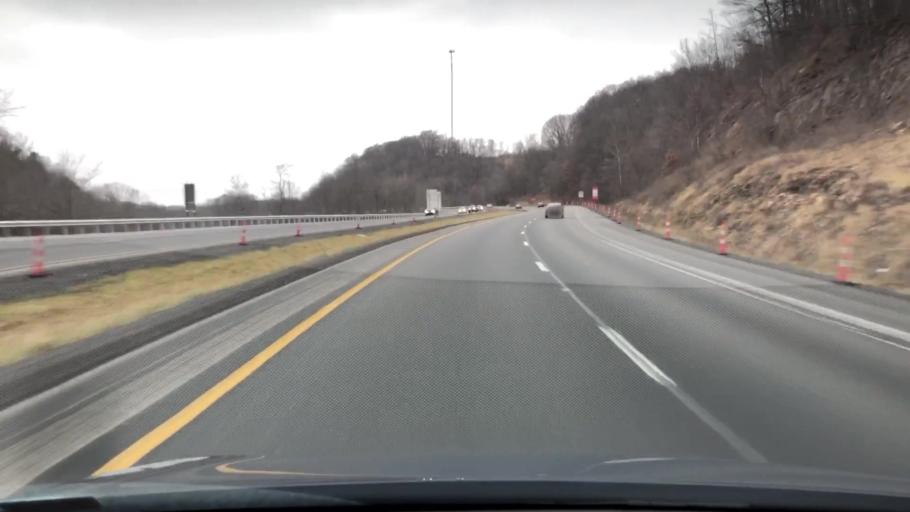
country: US
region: West Virginia
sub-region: Monongalia County
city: Star City
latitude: 39.6703
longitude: -80.0284
